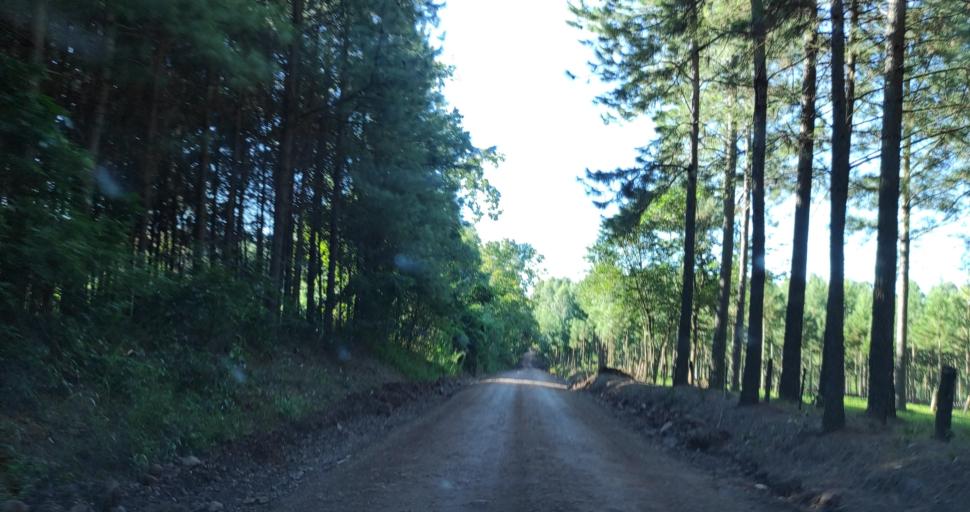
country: AR
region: Misiones
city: Garuhape
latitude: -26.8759
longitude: -54.9958
